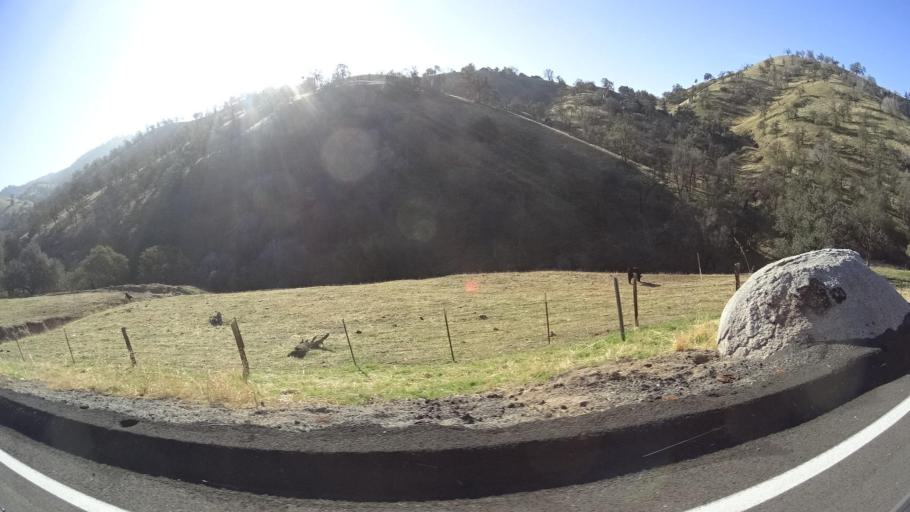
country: US
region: California
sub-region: Kern County
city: Alta Sierra
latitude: 35.7150
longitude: -118.8146
